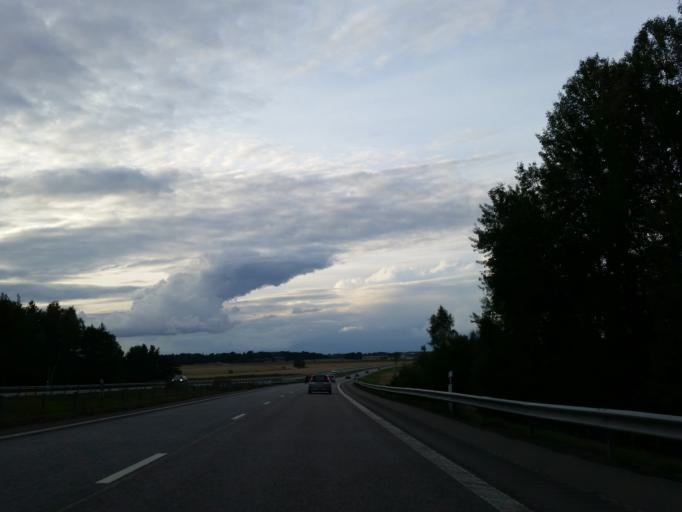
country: SE
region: Uppsala
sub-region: Uppsala Kommun
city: Alsike
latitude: 59.8042
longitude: 17.7638
